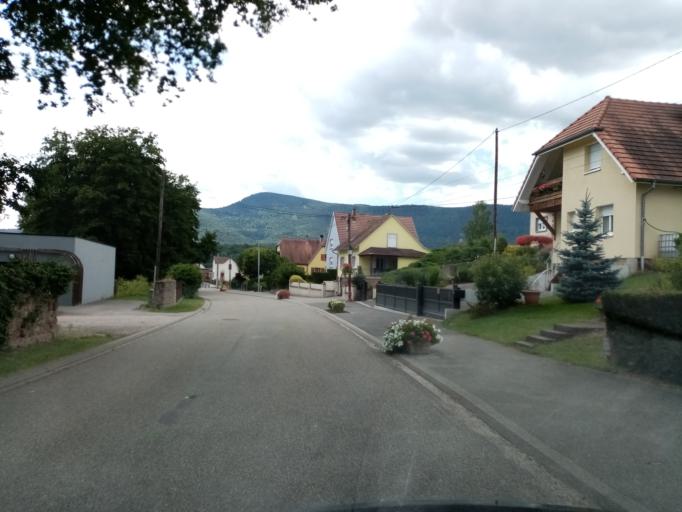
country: FR
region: Alsace
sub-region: Departement du Bas-Rhin
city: Ville
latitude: 48.3236
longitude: 7.3530
